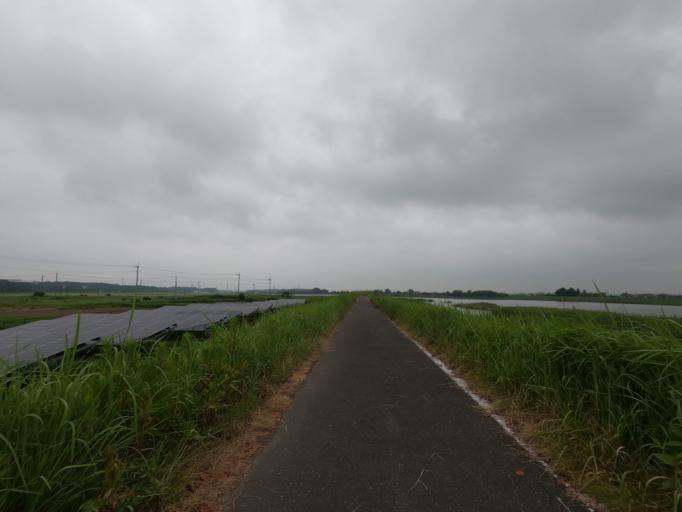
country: JP
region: Ibaraki
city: Moriya
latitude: 35.9328
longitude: 140.0418
